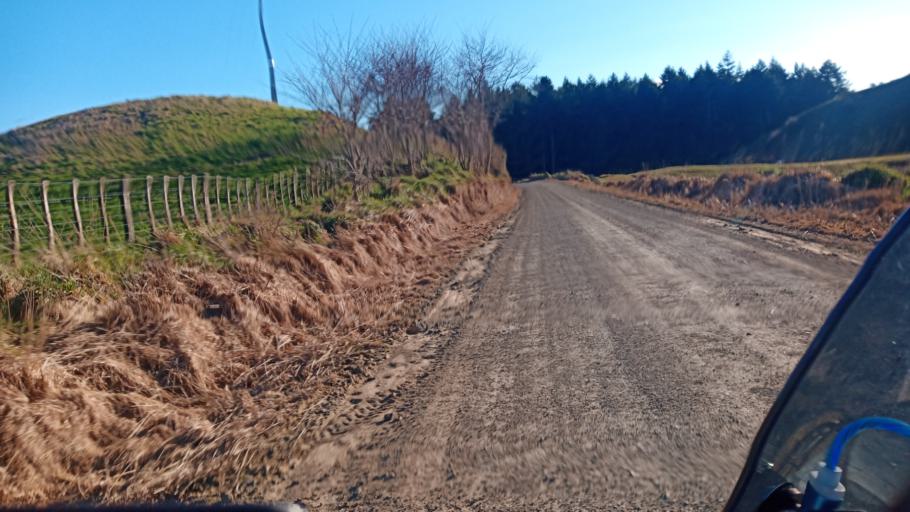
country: NZ
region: Bay of Plenty
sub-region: Opotiki District
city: Opotiki
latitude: -38.4594
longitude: 177.4273
